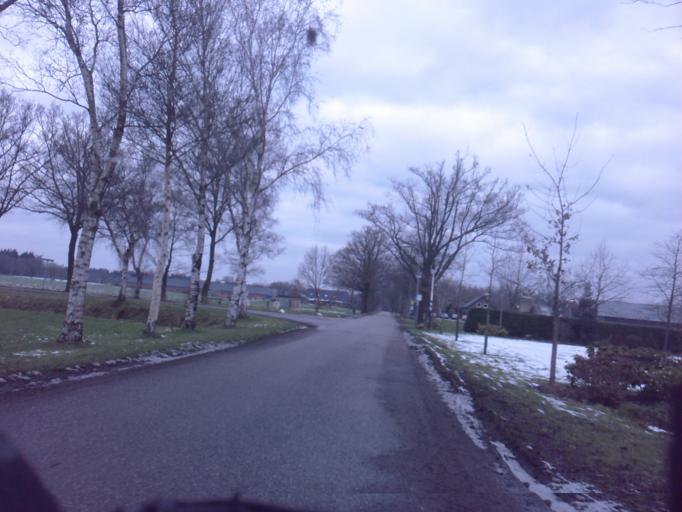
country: NL
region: Gelderland
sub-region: Gemeente Barneveld
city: Terschuur
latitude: 52.1075
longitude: 5.4990
